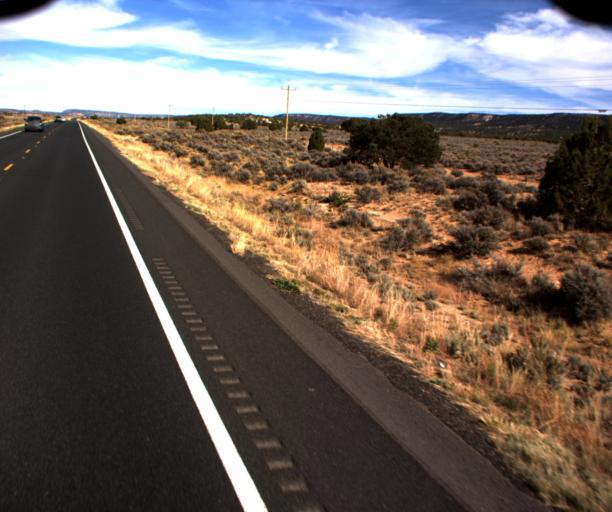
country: US
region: Arizona
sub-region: Navajo County
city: Kayenta
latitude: 36.5102
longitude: -110.6034
